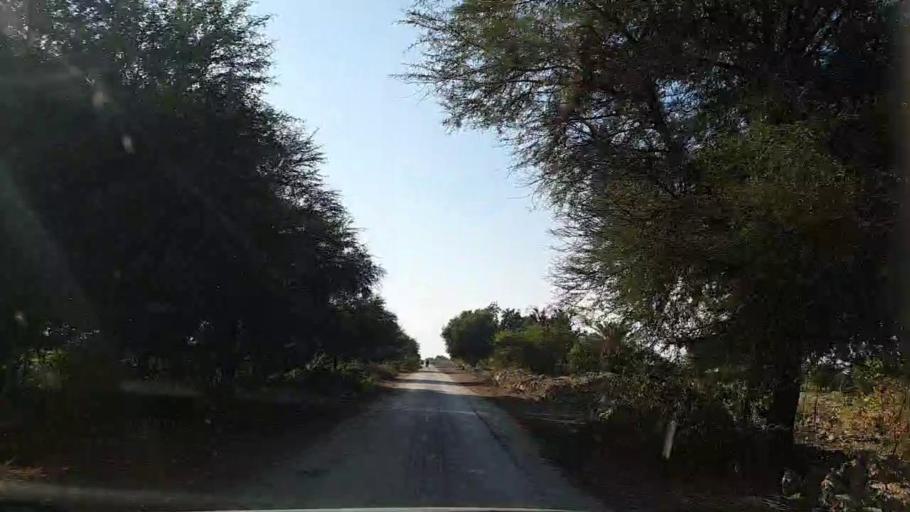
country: PK
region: Sindh
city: Pithoro
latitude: 25.6463
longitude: 69.3453
